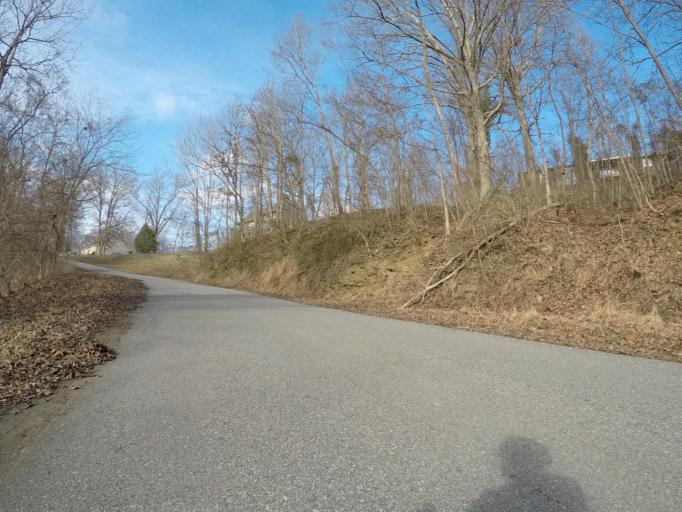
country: US
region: West Virginia
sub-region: Cabell County
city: Pea Ridge
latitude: 38.4315
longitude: -82.3379
